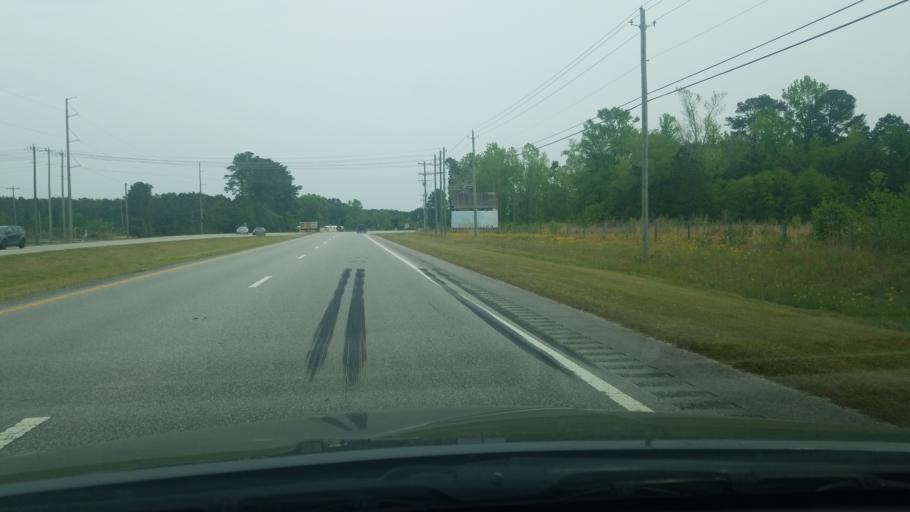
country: US
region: North Carolina
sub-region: Beaufort County
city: Washington
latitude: 35.4736
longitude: -77.1182
